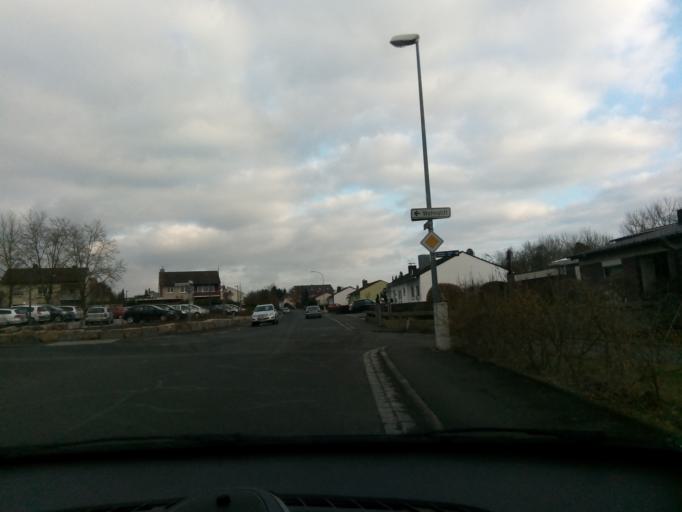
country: DE
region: Bavaria
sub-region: Regierungsbezirk Unterfranken
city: Gerolzhofen
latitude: 49.8936
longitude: 10.3447
